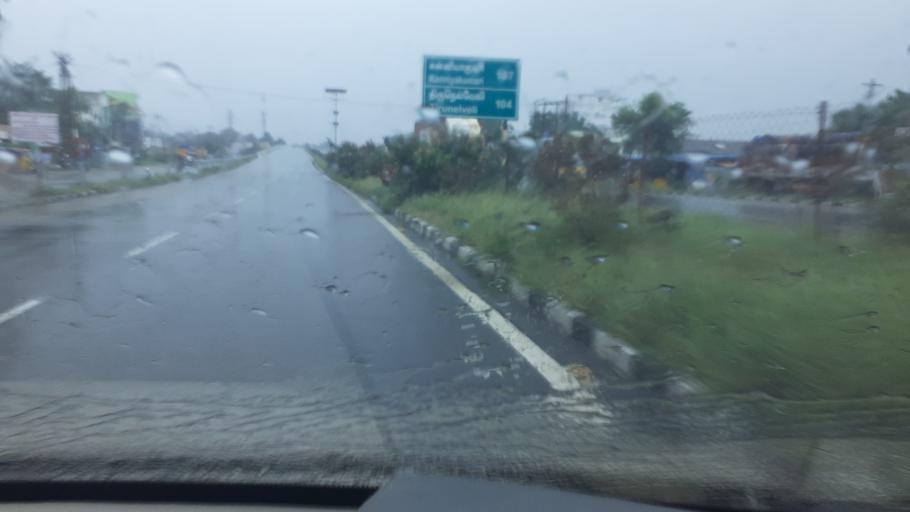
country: IN
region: Tamil Nadu
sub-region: Virudhunagar
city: Virudunagar
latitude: 9.6055
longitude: 77.9552
